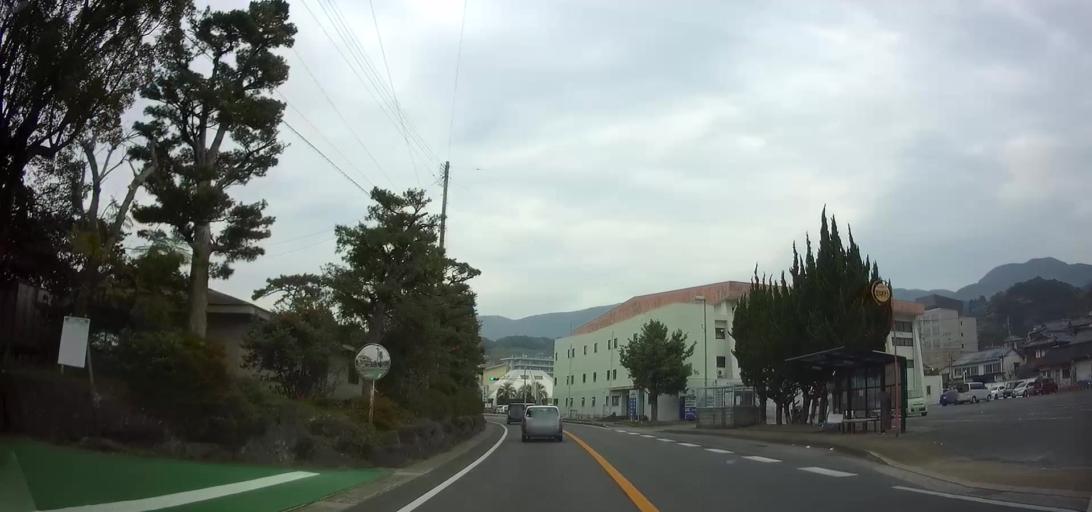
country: JP
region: Nagasaki
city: Shimabara
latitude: 32.7194
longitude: 130.2011
